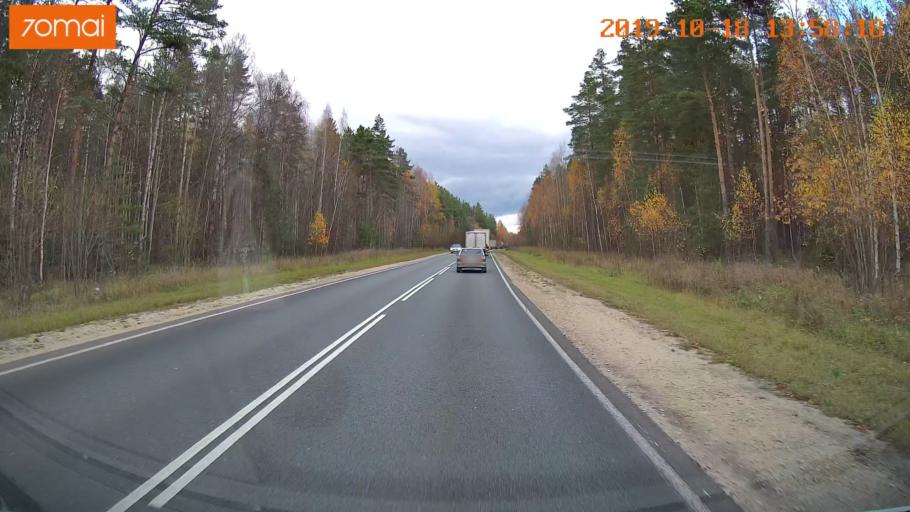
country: RU
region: Rjazan
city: Spas-Klepiki
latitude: 55.0833
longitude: 40.0532
